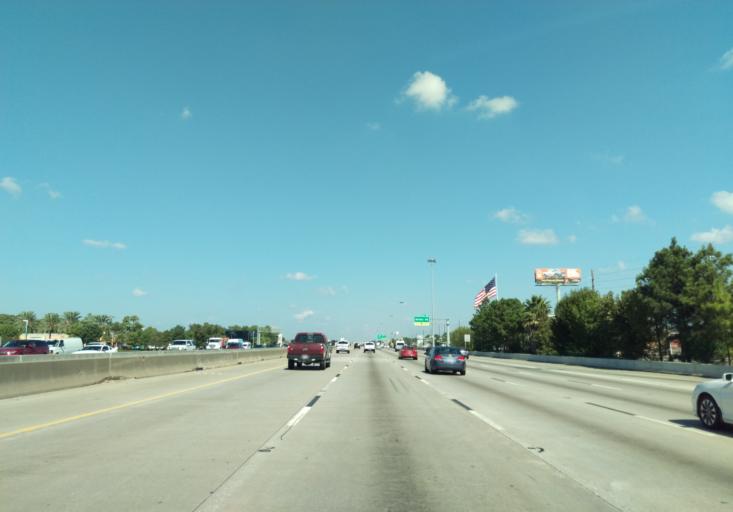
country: US
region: Texas
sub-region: Harris County
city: Aldine
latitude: 29.9876
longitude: -95.4236
